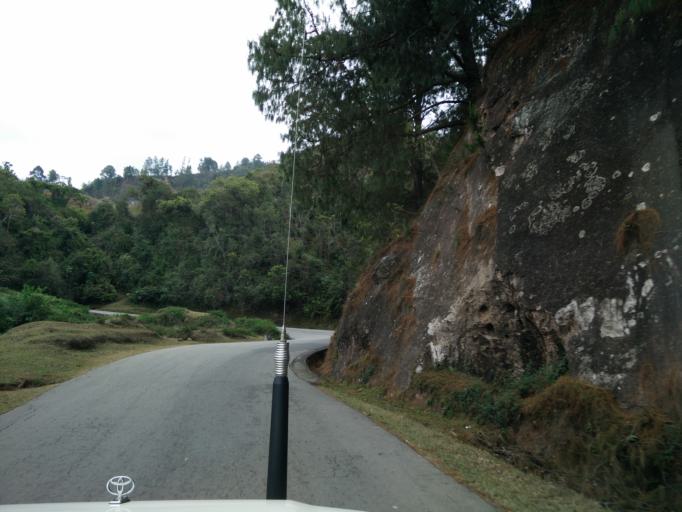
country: MG
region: Upper Matsiatra
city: Fianarantsoa
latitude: -21.2883
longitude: 47.2436
